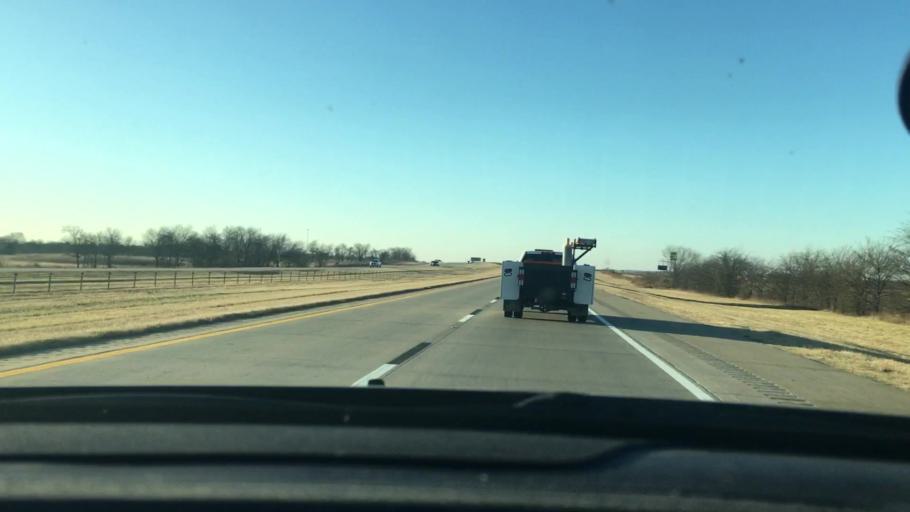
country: US
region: Oklahoma
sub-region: Carter County
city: Ardmore
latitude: 34.3403
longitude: -97.1495
